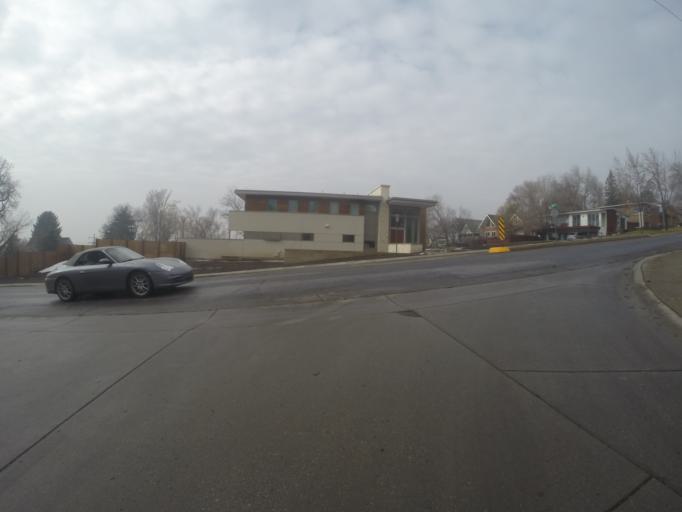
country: US
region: Utah
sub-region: Salt Lake County
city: Salt Lake City
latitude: 40.7749
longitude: -111.8520
